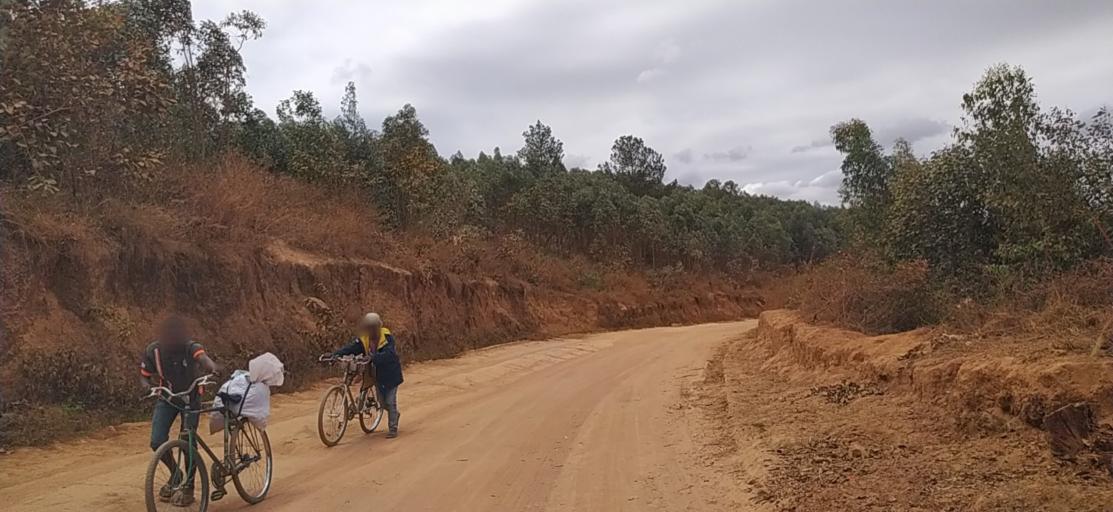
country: MG
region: Alaotra Mangoro
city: Ambatondrazaka
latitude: -18.0064
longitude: 48.2593
